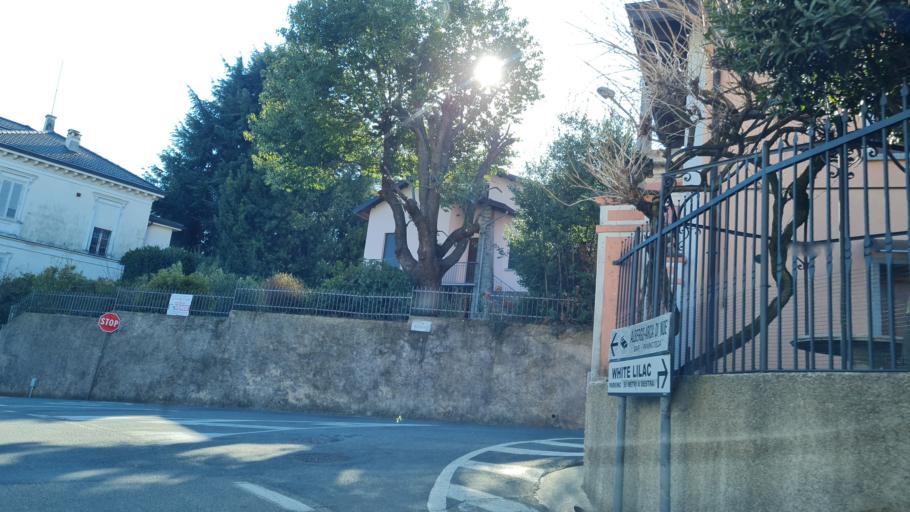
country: IT
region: Piedmont
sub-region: Provincia di Novara
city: Meina
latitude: 45.7815
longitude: 8.5361
